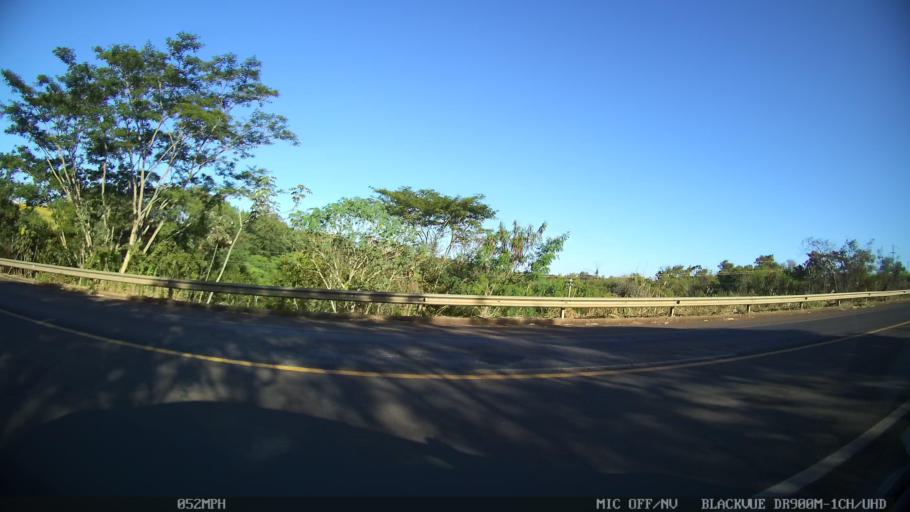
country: BR
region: Sao Paulo
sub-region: Olimpia
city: Olimpia
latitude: -20.6952
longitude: -48.9270
